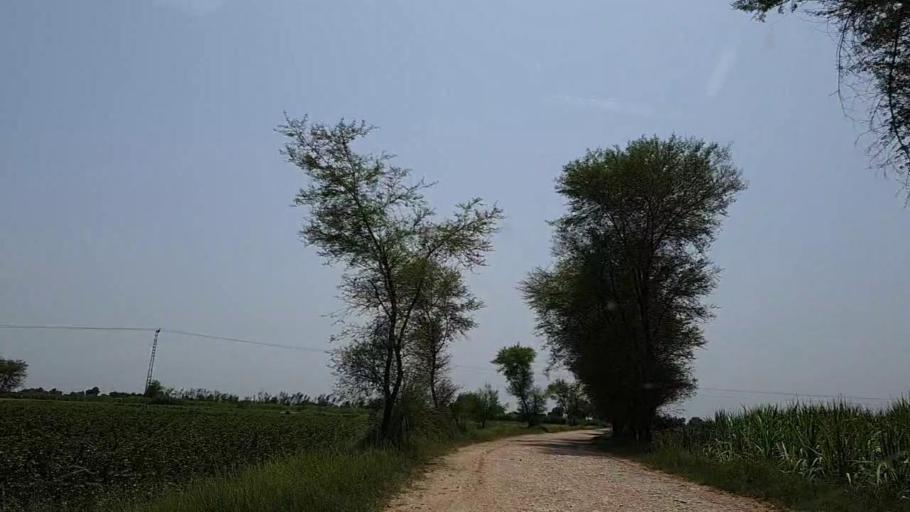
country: PK
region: Sindh
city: Ghotki
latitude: 27.9752
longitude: 69.4003
